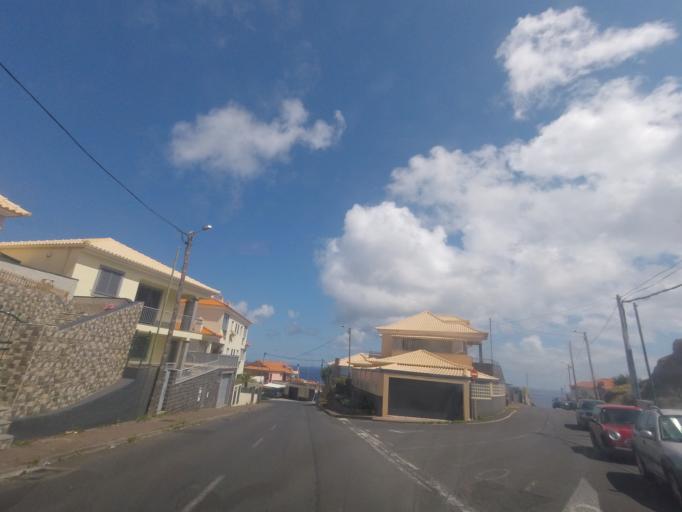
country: PT
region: Madeira
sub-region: Machico
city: Canical
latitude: 32.7425
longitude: -16.7418
